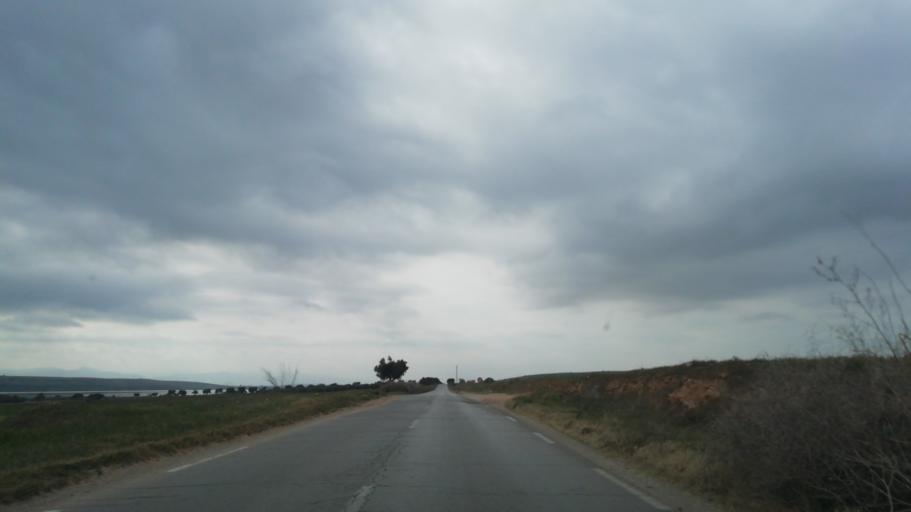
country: DZ
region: Oran
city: Sidi ech Chahmi
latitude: 35.6197
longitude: -0.4137
